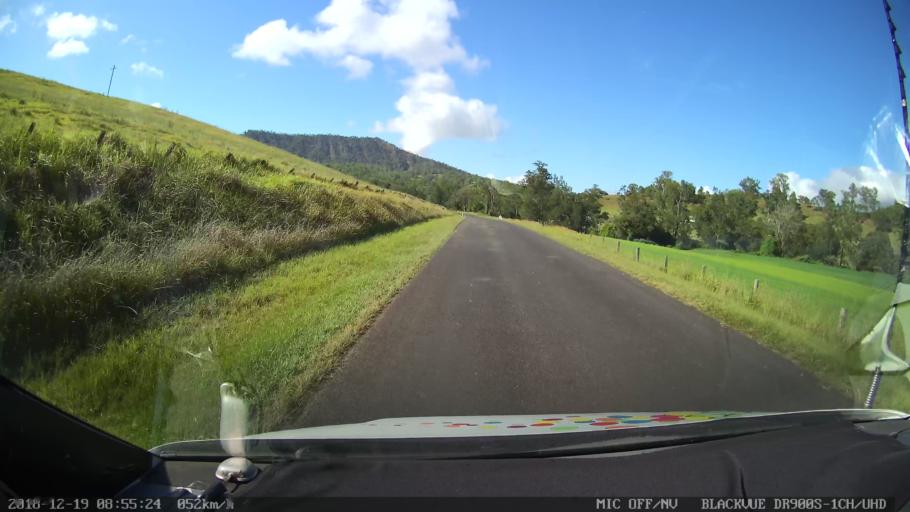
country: AU
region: New South Wales
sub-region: Kyogle
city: Kyogle
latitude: -28.4141
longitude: 152.9781
